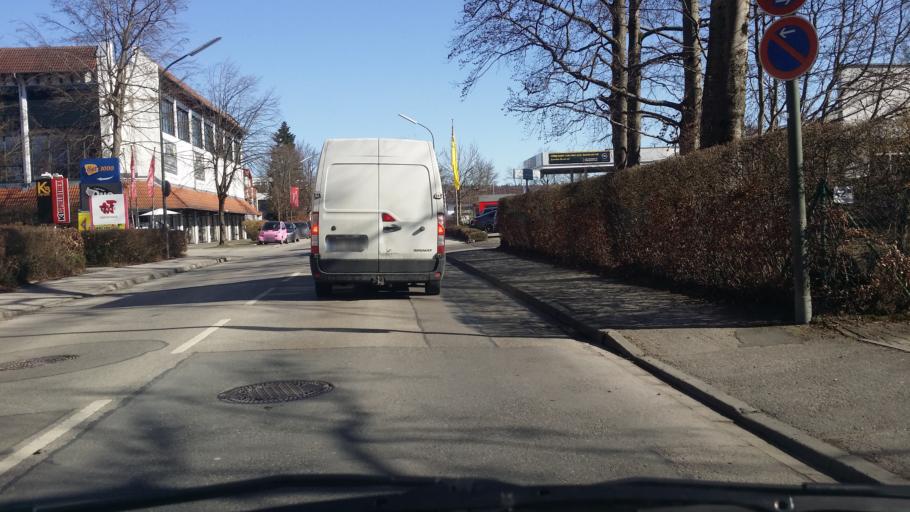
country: DE
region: Bavaria
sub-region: Upper Bavaria
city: Geretsried
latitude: 47.8557
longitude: 11.4888
